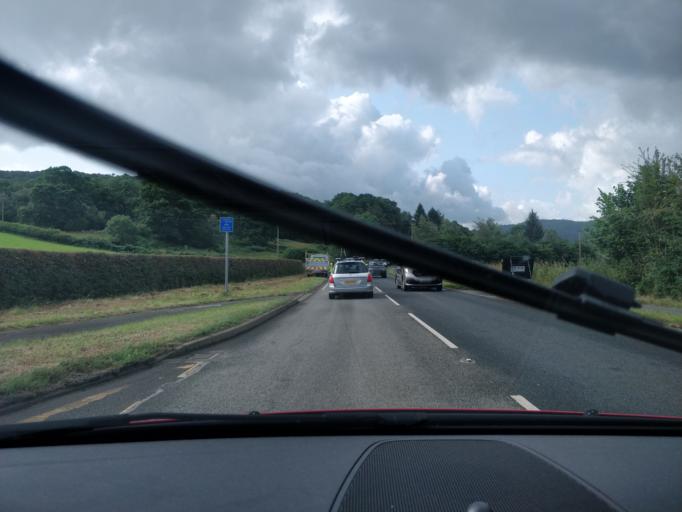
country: GB
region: Wales
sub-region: Conwy
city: Betws-y-Coed
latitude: 53.1106
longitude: -3.7827
